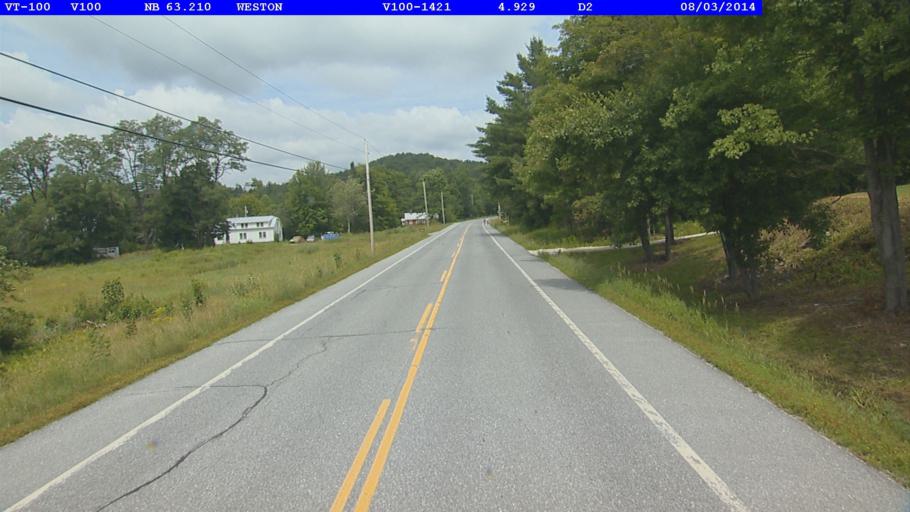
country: US
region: Vermont
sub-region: Windsor County
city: Chester
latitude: 43.3152
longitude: -72.7873
